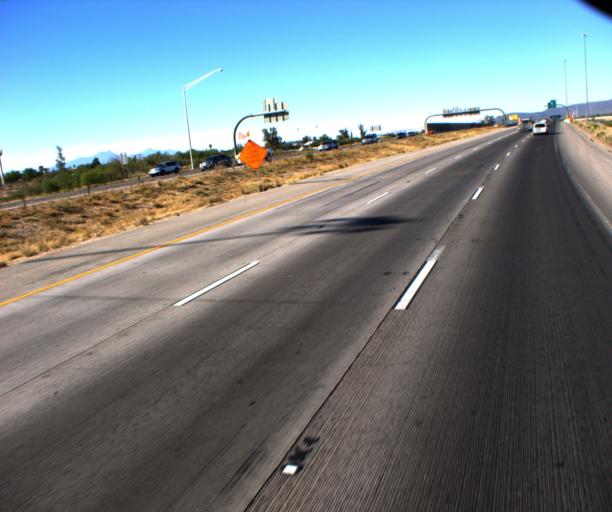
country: US
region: Arizona
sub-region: Pima County
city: South Tucson
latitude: 32.1921
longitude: -110.9803
